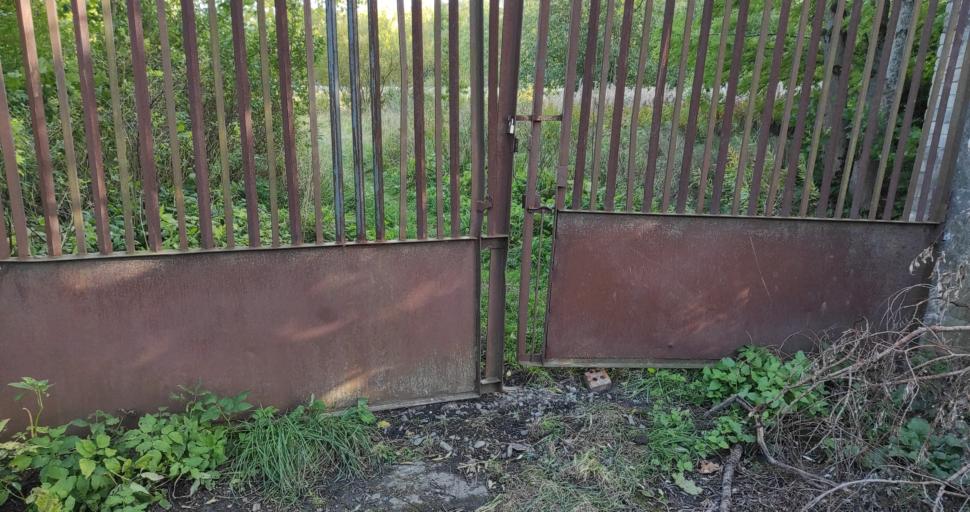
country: RU
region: St.-Petersburg
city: Pushkin
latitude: 59.7273
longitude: 30.3740
